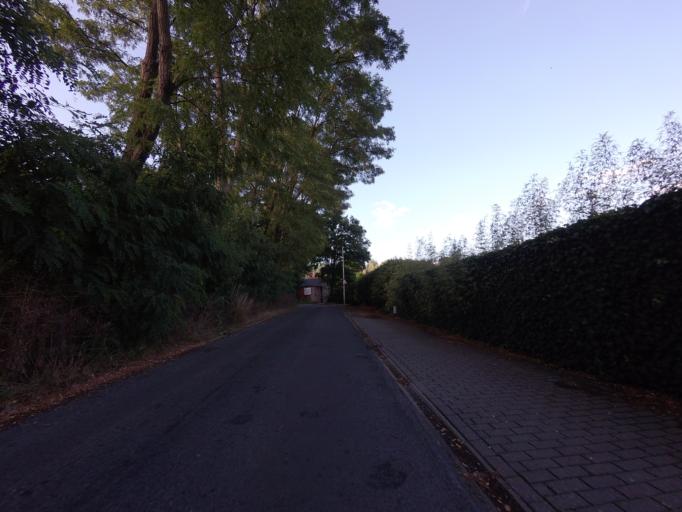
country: BE
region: Flanders
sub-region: Provincie Antwerpen
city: Edegem
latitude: 51.1476
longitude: 4.4389
